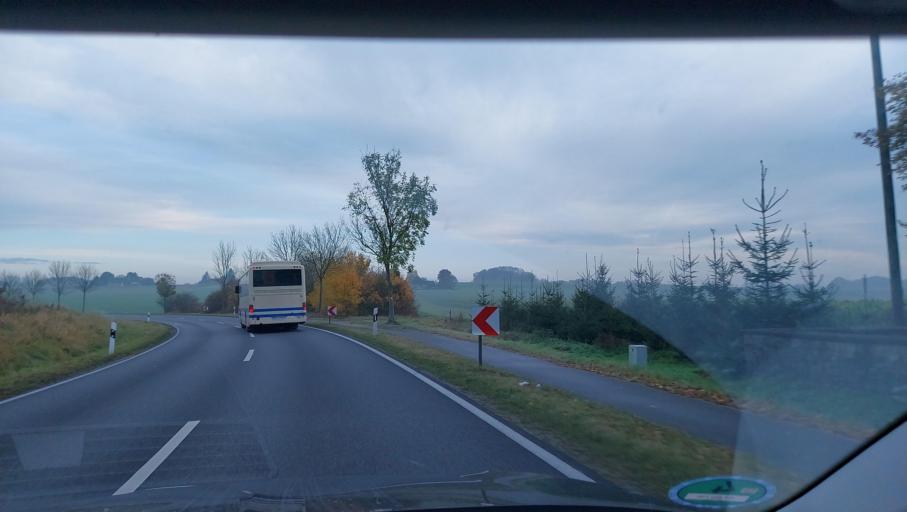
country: DE
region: North Rhine-Westphalia
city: Halle
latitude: 52.0942
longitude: 8.3729
